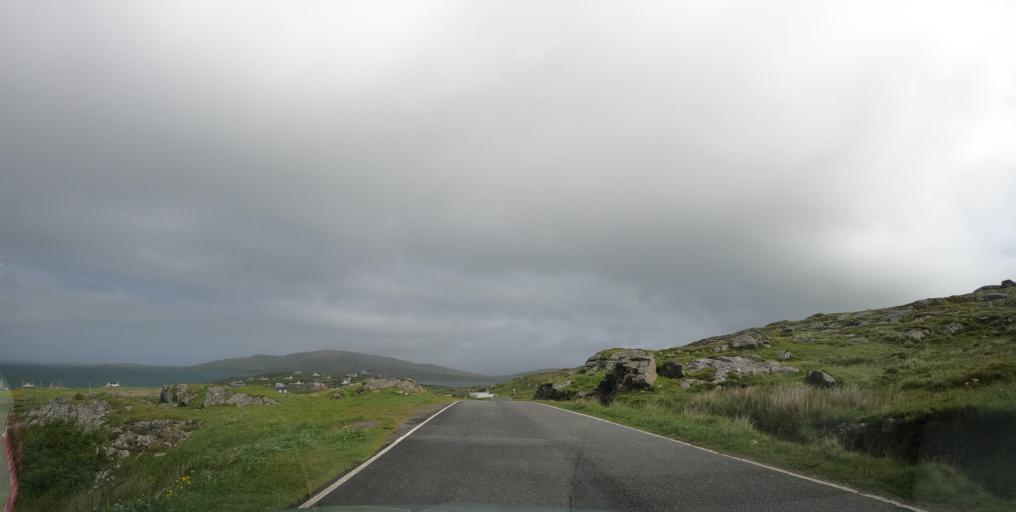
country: GB
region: Scotland
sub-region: Eilean Siar
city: Isle of South Uist
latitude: 57.0796
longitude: -7.3022
